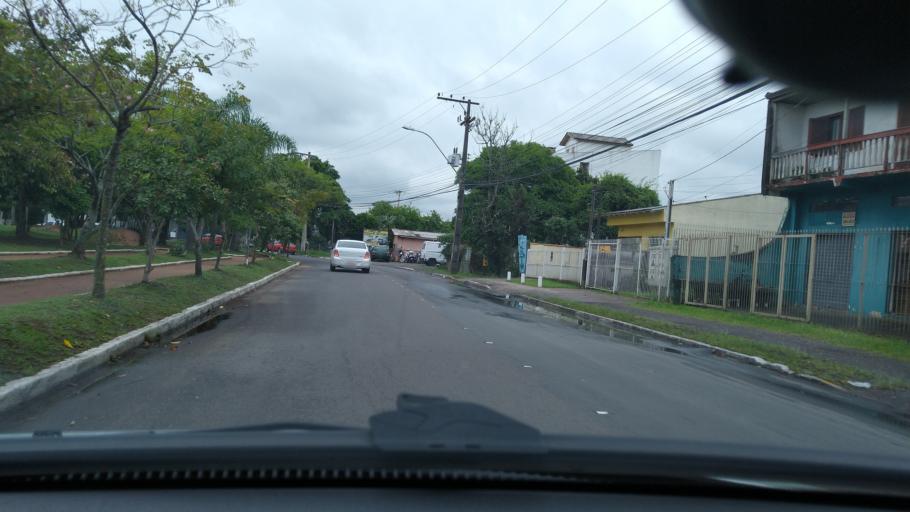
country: BR
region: Rio Grande do Sul
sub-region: Canoas
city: Canoas
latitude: -29.9014
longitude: -51.2046
